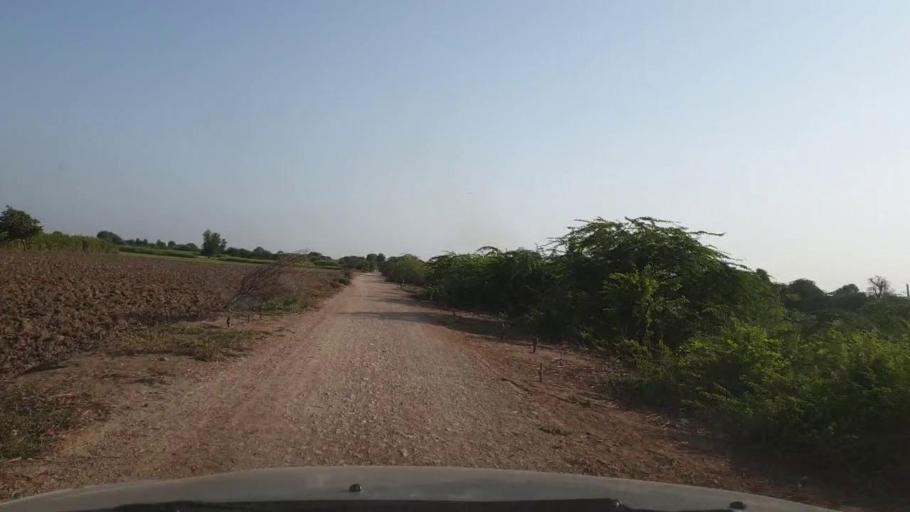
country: PK
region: Sindh
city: Tando Ghulam Ali
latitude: 25.1209
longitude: 68.9407
